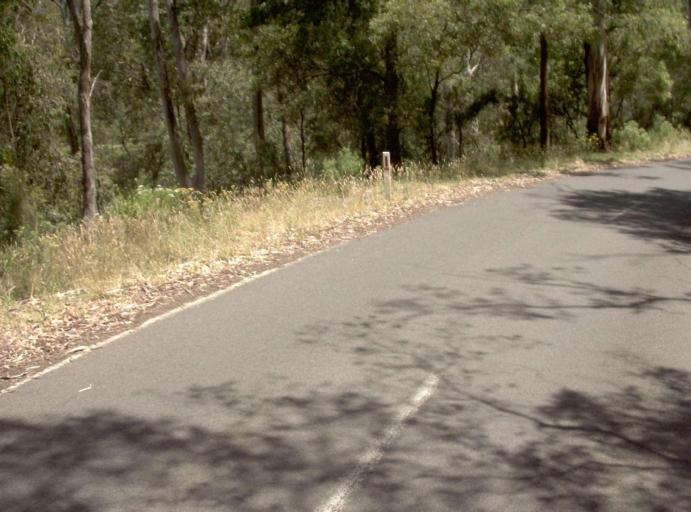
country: AU
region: Victoria
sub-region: Latrobe
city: Traralgon
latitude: -37.9519
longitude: 146.4322
